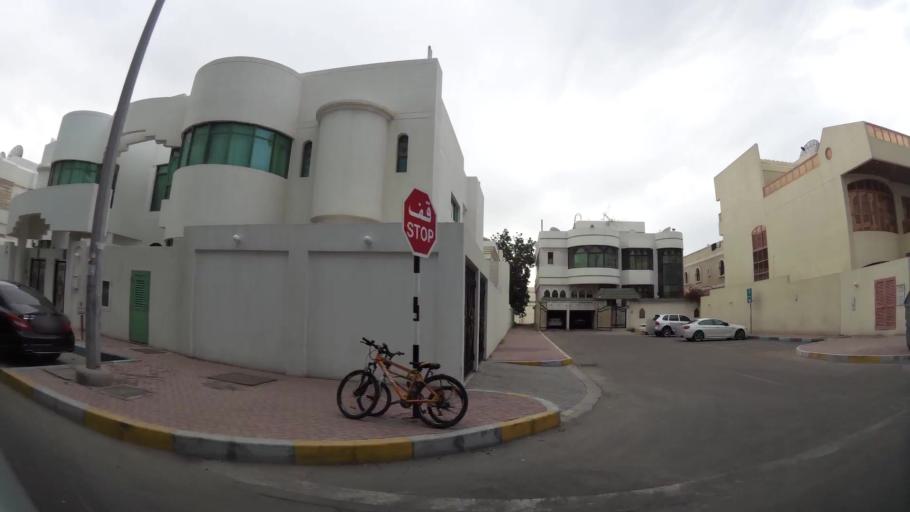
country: AE
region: Abu Dhabi
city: Abu Dhabi
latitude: 24.4807
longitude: 54.3775
